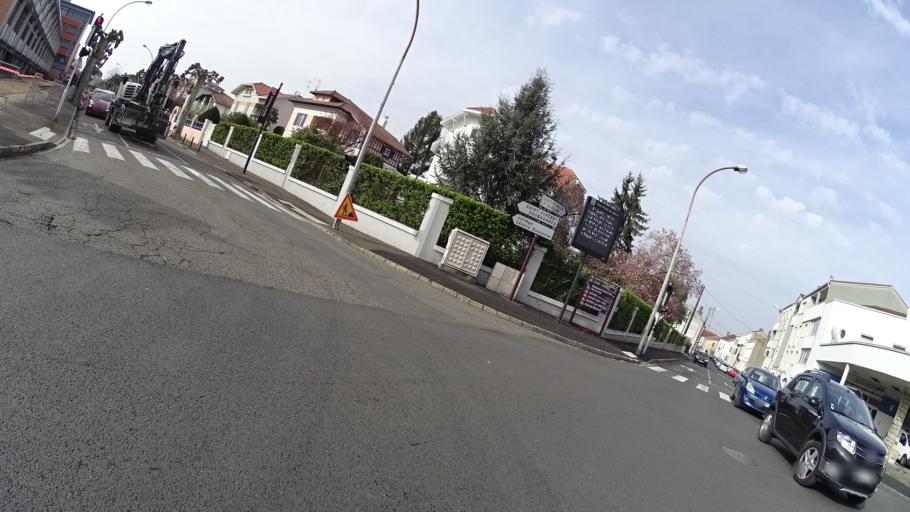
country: FR
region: Aquitaine
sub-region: Departement des Landes
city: Dax
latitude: 43.7032
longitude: -1.0531
